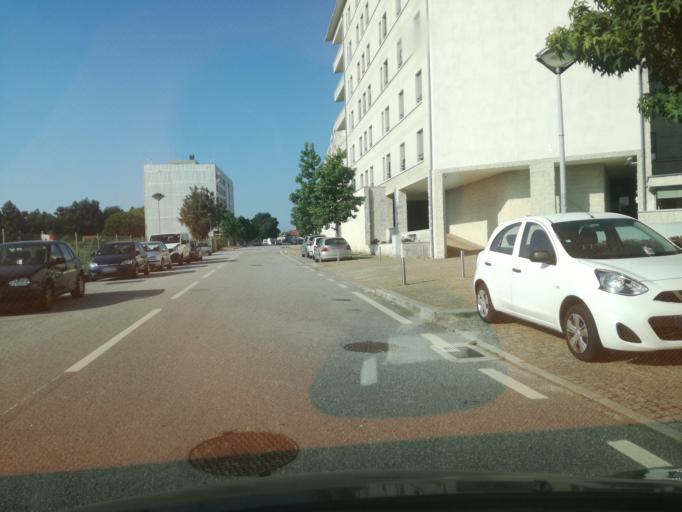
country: PT
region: Porto
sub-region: Maia
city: Gemunde
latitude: 41.2602
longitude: -8.6662
